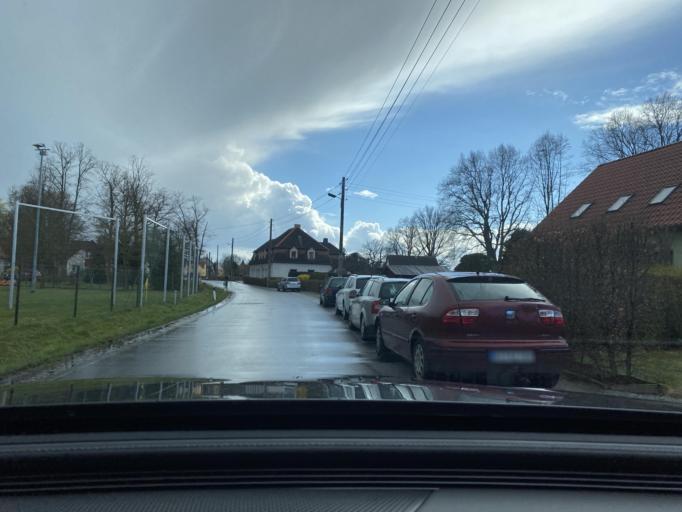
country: DE
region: Saxony
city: Grossdubrau
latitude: 51.3022
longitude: 14.4560
